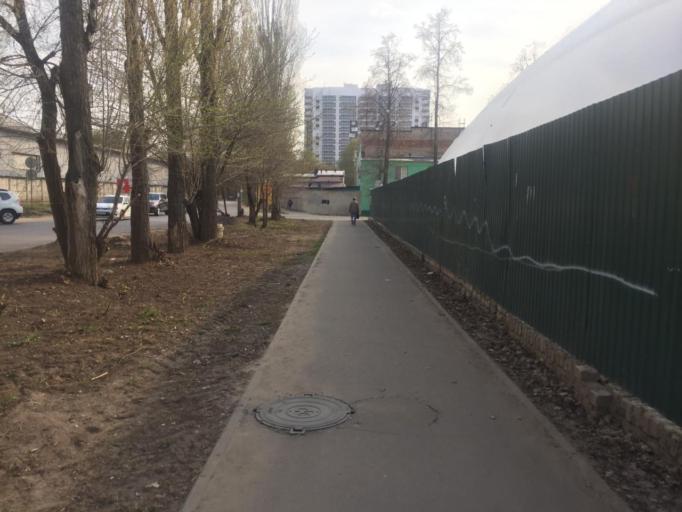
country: RU
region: Voronezj
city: Voronezh
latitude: 51.6783
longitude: 39.1448
